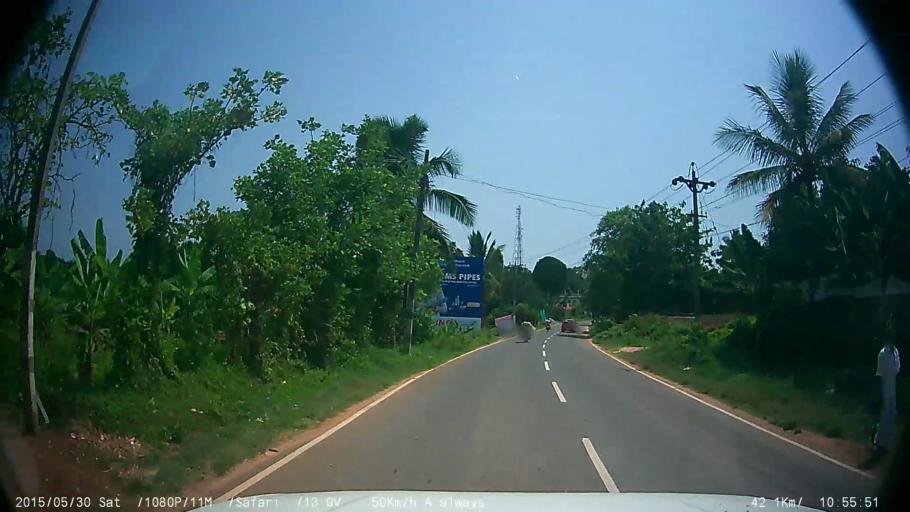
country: IN
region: Kerala
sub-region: Wayanad
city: Kalpetta
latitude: 11.6694
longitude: 76.0793
